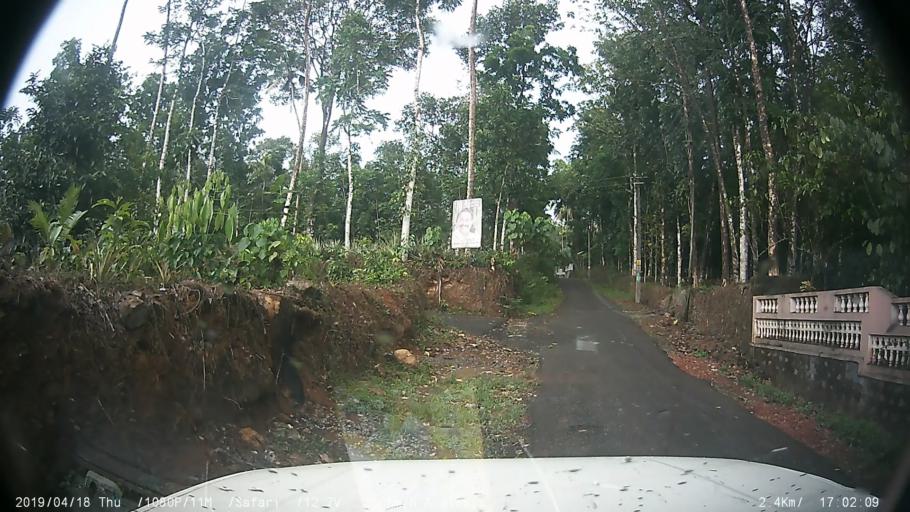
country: IN
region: Kerala
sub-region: Kottayam
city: Palackattumala
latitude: 9.7783
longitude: 76.5882
